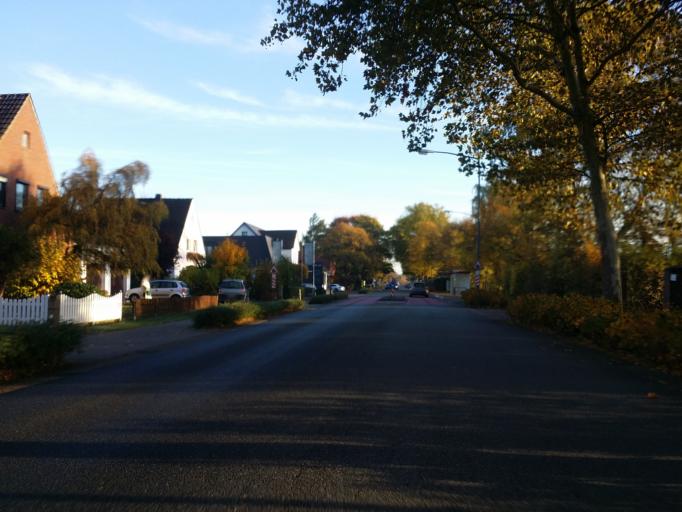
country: DE
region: Lower Saxony
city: Stuhr
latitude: 53.0064
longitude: 8.7821
